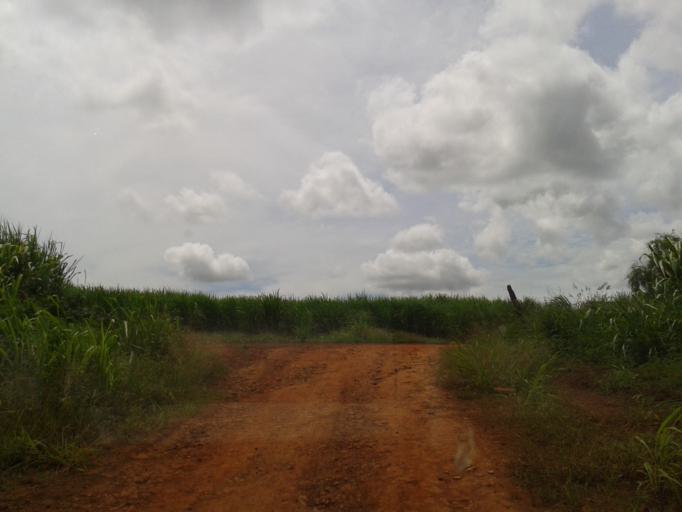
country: BR
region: Minas Gerais
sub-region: Centralina
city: Centralina
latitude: -18.5895
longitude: -49.2707
